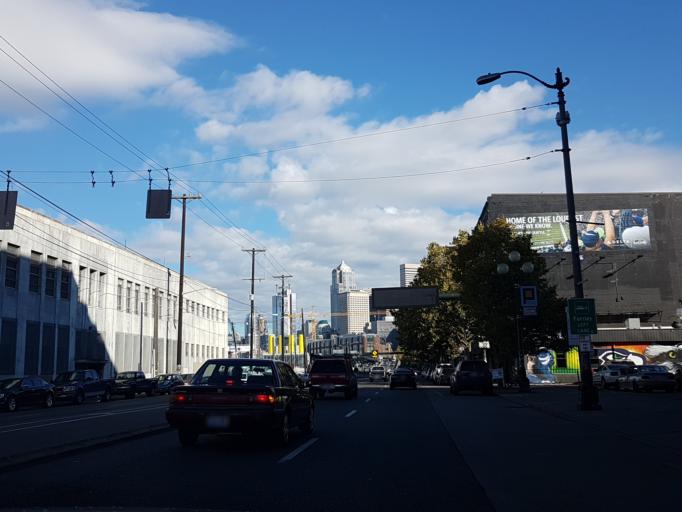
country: US
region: Washington
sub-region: King County
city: Seattle
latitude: 47.5927
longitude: -122.3342
